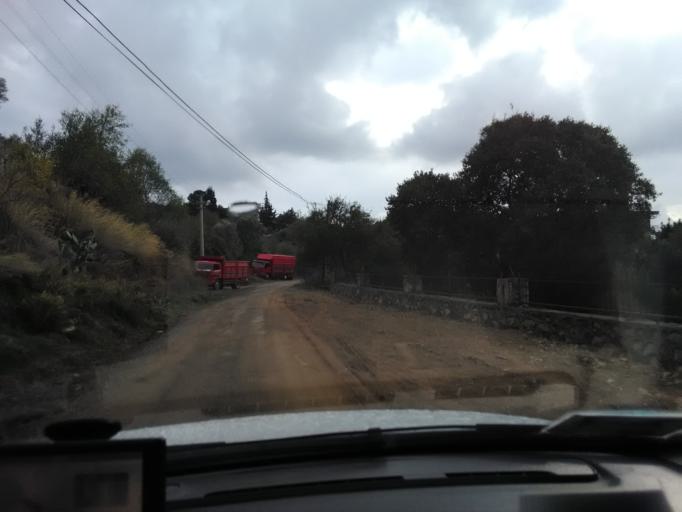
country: TR
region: Antalya
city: Gazipasa
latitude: 36.1569
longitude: 32.4252
